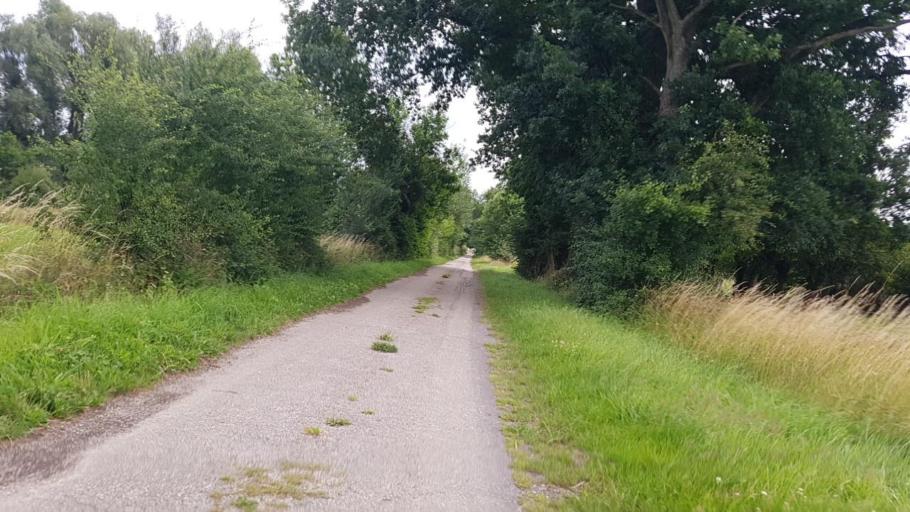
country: FR
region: Picardie
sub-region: Departement de l'Aisne
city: Esqueheries
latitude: 49.9072
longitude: 3.7755
